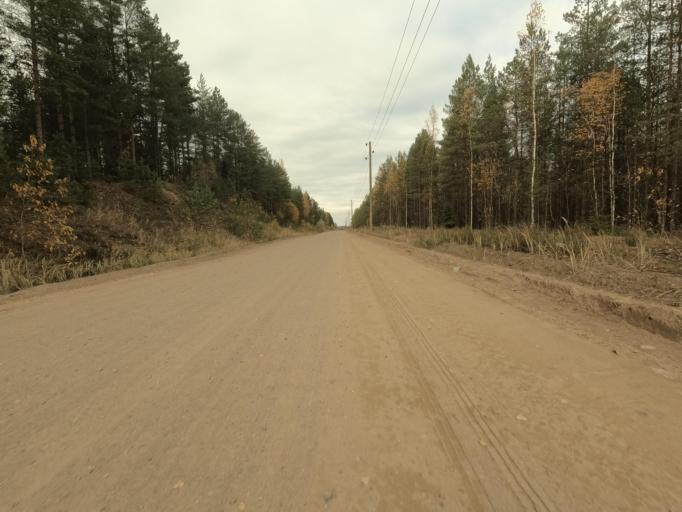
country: RU
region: Leningrad
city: Priladozhskiy
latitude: 59.6955
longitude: 31.3616
